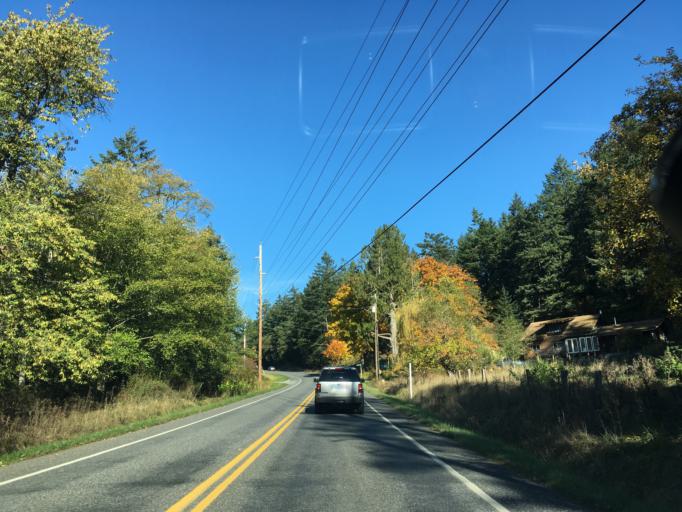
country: US
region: Washington
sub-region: San Juan County
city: Friday Harbor
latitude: 48.6124
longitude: -122.9448
